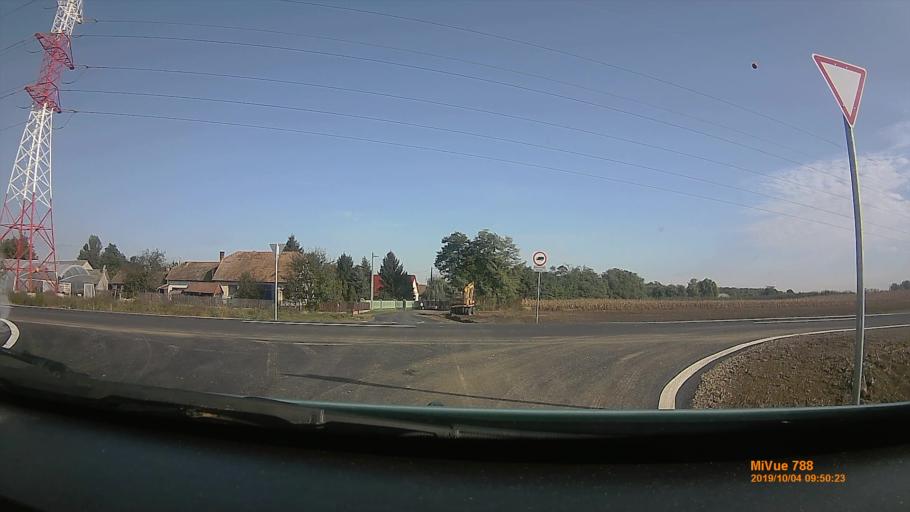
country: HU
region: Szabolcs-Szatmar-Bereg
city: Nyiregyhaza
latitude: 47.9431
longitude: 21.6582
